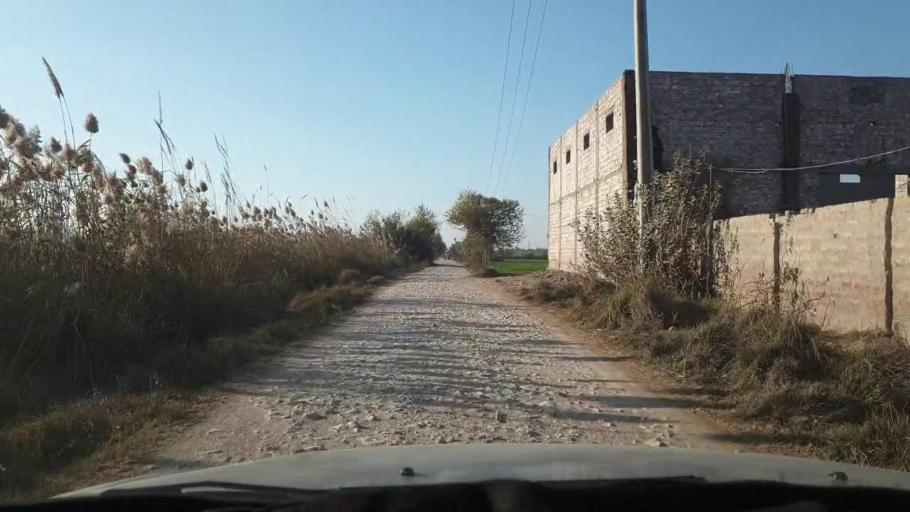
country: PK
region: Sindh
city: Adilpur
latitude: 27.9503
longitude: 69.2355
